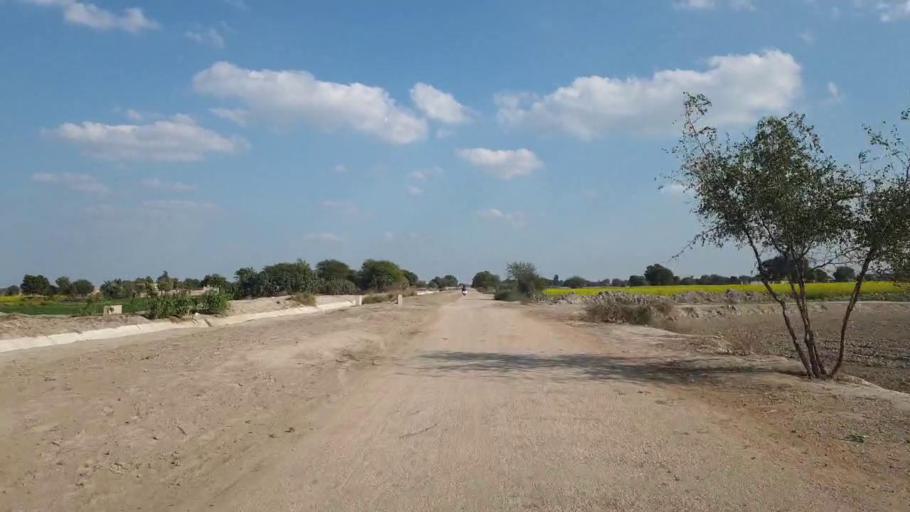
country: PK
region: Sindh
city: Shahpur Chakar
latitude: 26.1045
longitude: 68.5861
